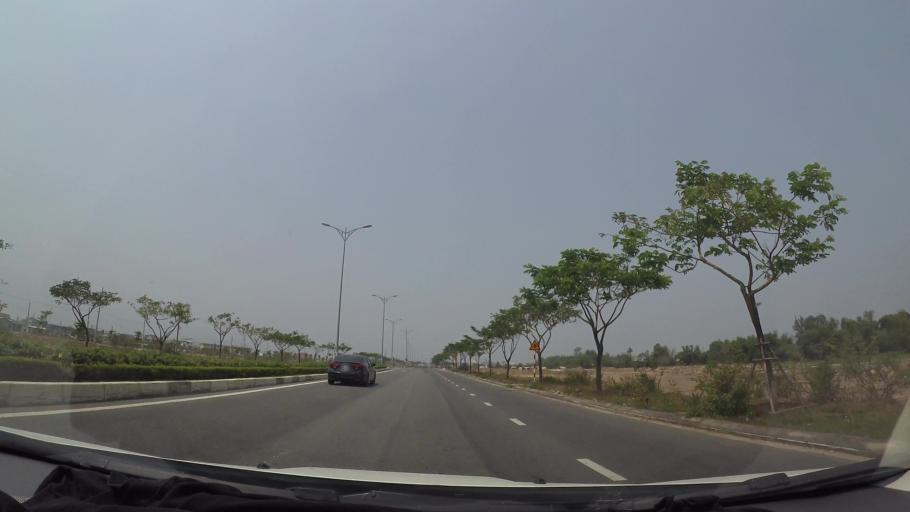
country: VN
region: Da Nang
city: Ngu Hanh Son
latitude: 15.9900
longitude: 108.2383
